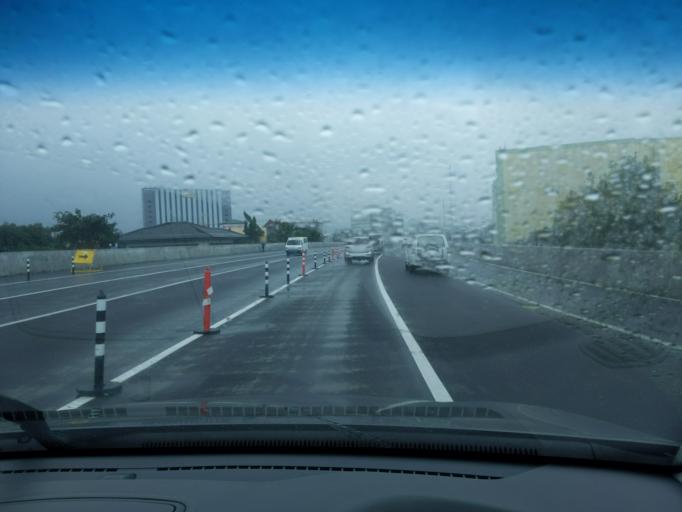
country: PH
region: Metro Manila
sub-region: San Juan
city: San Juan
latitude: 14.5915
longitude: 121.0236
